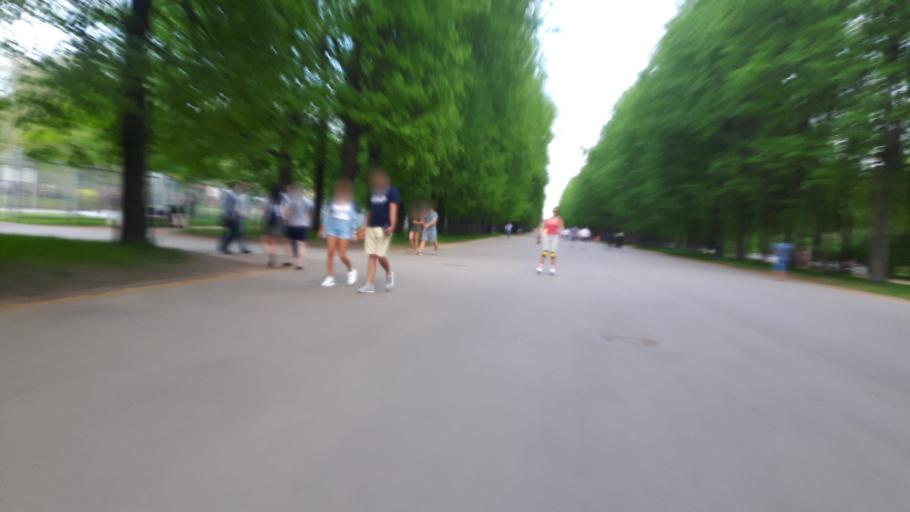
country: RU
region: Leningrad
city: Krestovskiy ostrov
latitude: 59.9718
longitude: 30.2462
